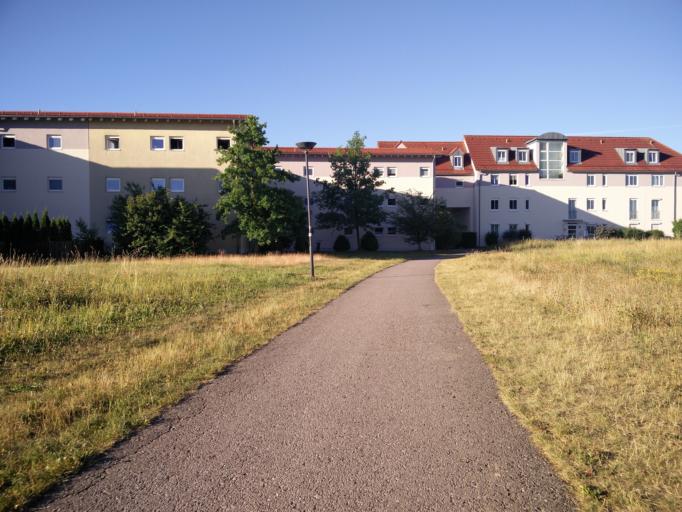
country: DE
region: Bavaria
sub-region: Upper Bavaria
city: Unterhaching
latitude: 48.0864
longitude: 11.6277
